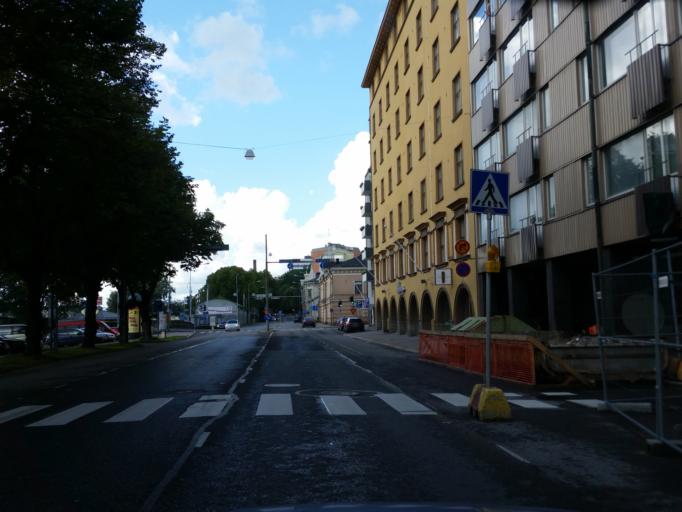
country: FI
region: Varsinais-Suomi
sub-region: Turku
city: Turku
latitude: 60.4456
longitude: 22.2564
